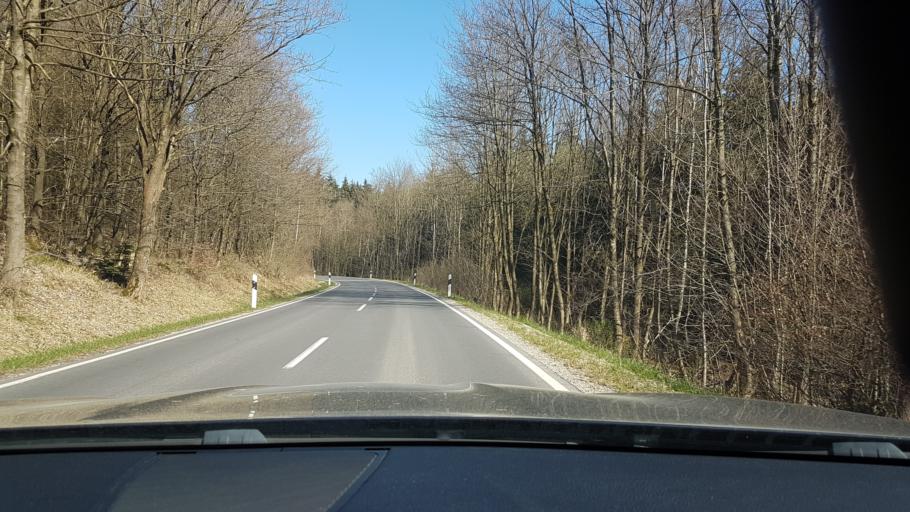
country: DE
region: Lower Saxony
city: Coppenbrugge
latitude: 52.1459
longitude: 9.5971
